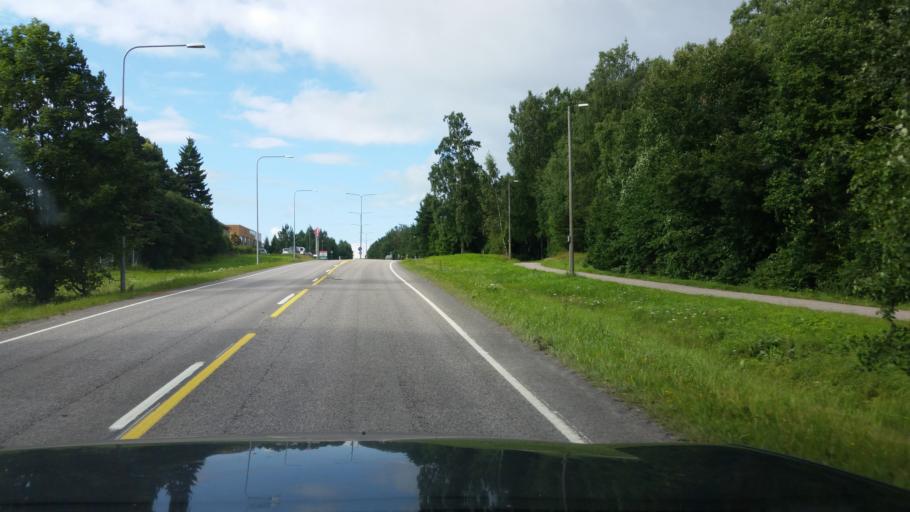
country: FI
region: Uusimaa
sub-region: Helsinki
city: Vantaa
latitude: 60.2255
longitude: 25.1179
